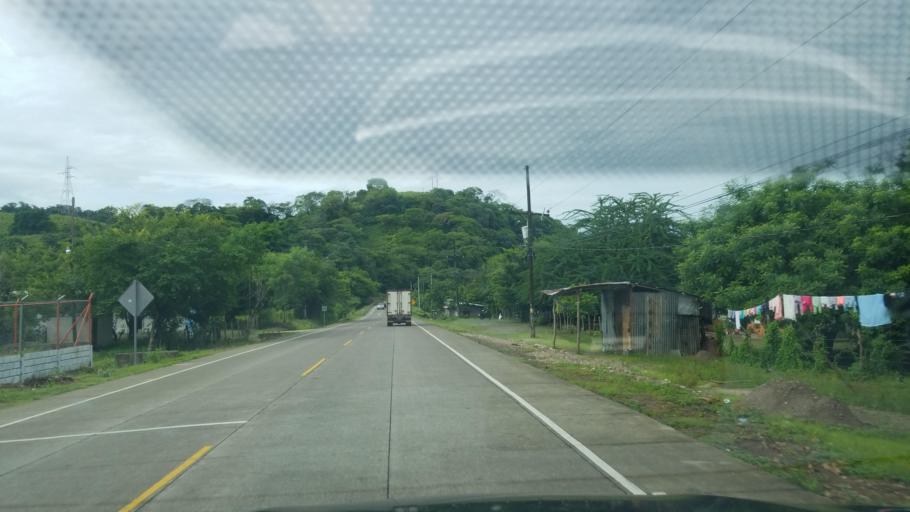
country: HN
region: Choluteca
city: Pespire
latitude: 13.6354
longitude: -87.3691
